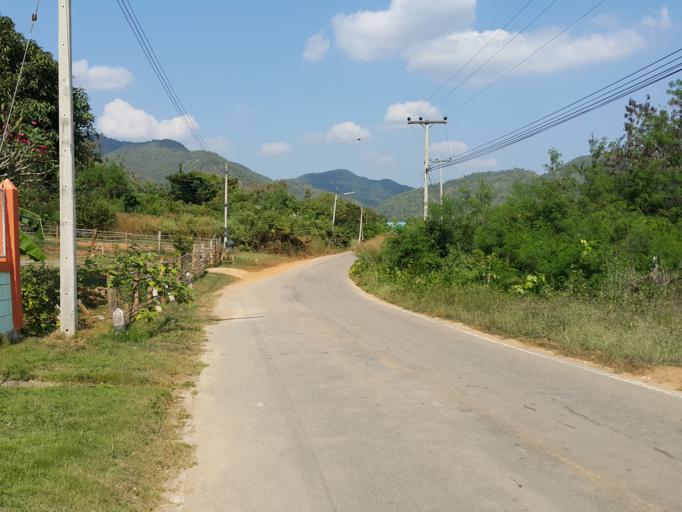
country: TH
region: Sukhothai
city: Thung Saliam
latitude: 17.3381
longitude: 99.4596
